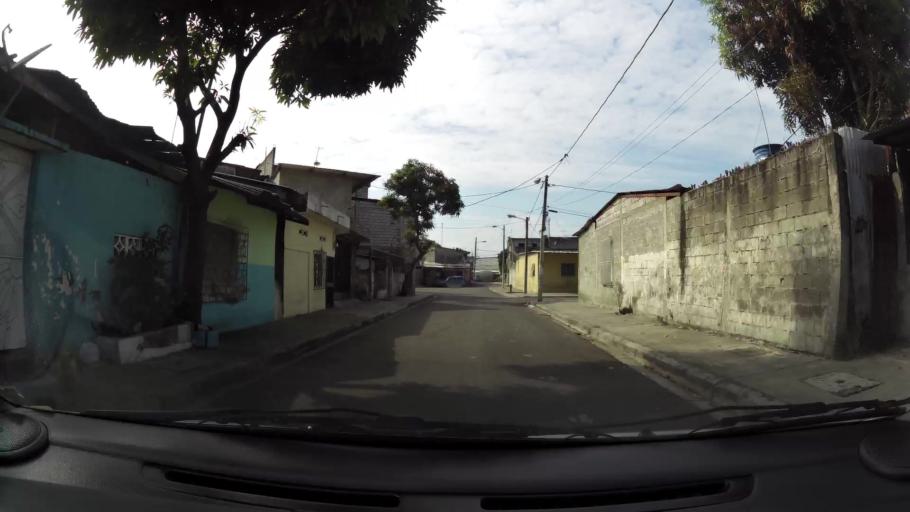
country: EC
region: Guayas
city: Guayaquil
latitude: -2.2582
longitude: -79.8809
